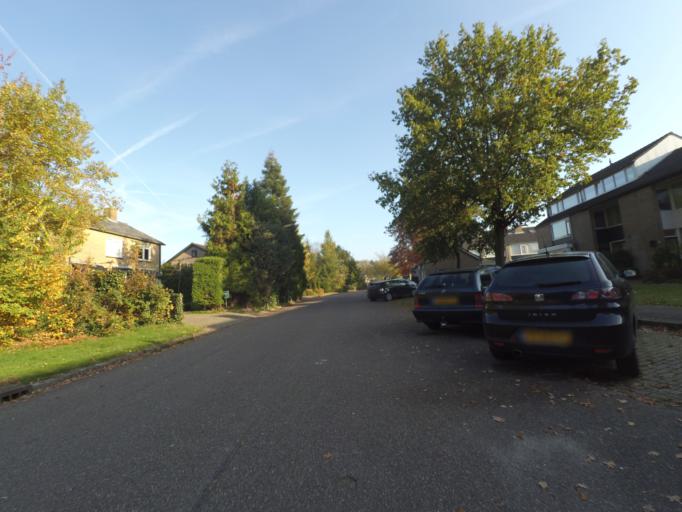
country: NL
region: Utrecht
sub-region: Gemeente Leusden
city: Leusden
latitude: 52.1383
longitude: 5.4331
